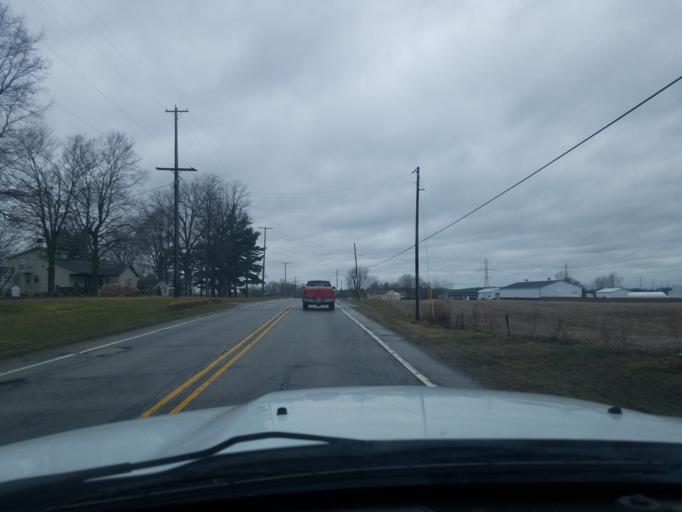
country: US
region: Indiana
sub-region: Noble County
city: Rome City
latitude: 41.4529
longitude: -85.3828
